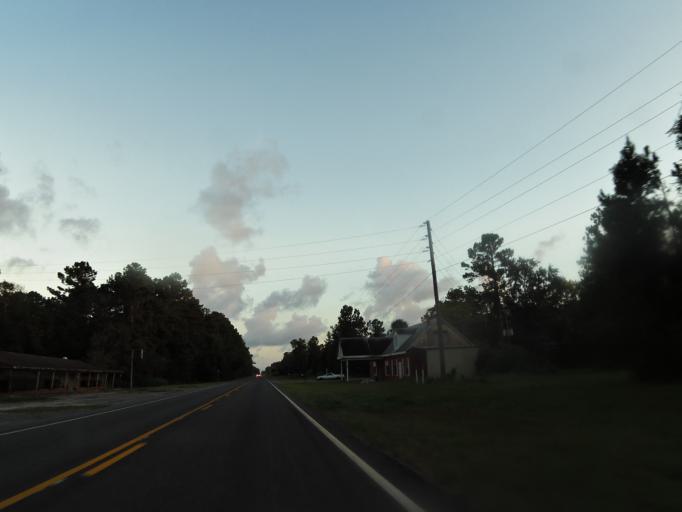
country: US
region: Georgia
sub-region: Camden County
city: Kingsland
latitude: 30.8288
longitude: -81.6960
